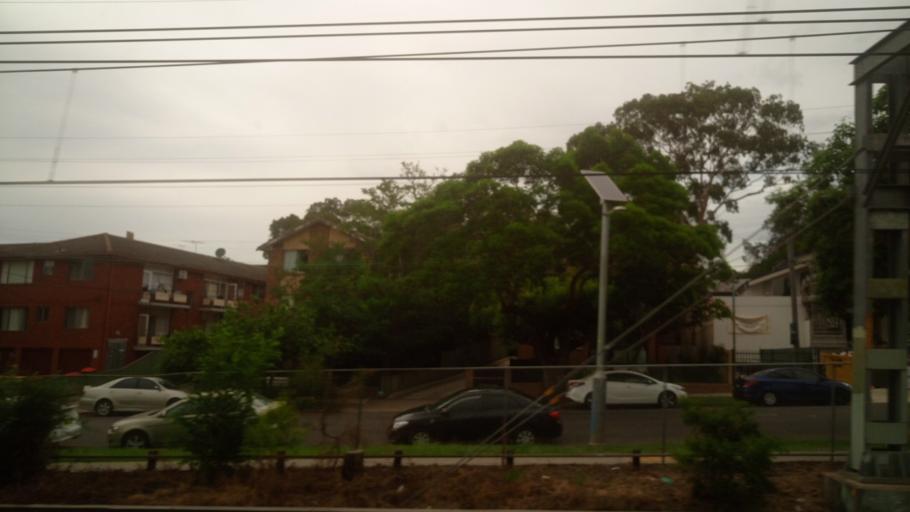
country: AU
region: New South Wales
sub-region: Strathfield
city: Homebush
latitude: -33.8643
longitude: 151.0676
